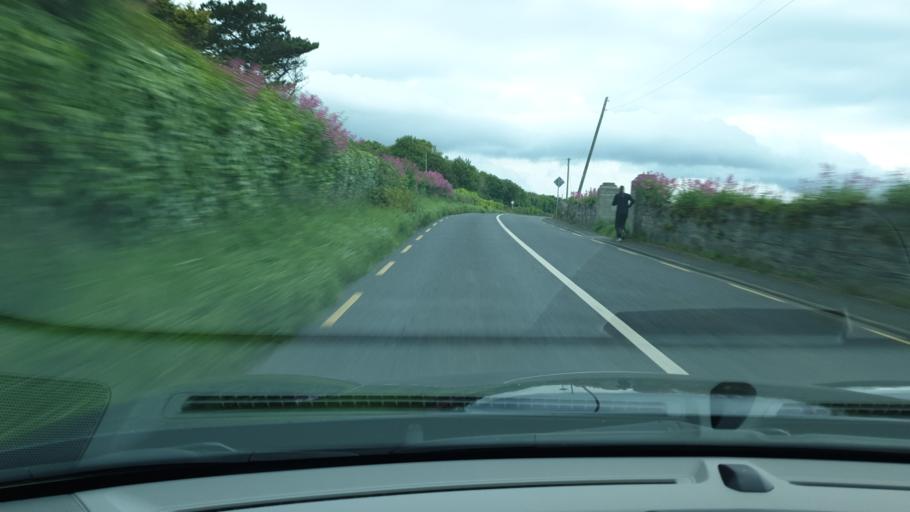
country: IE
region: Leinster
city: Balrothery
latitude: 53.5855
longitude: -6.1489
